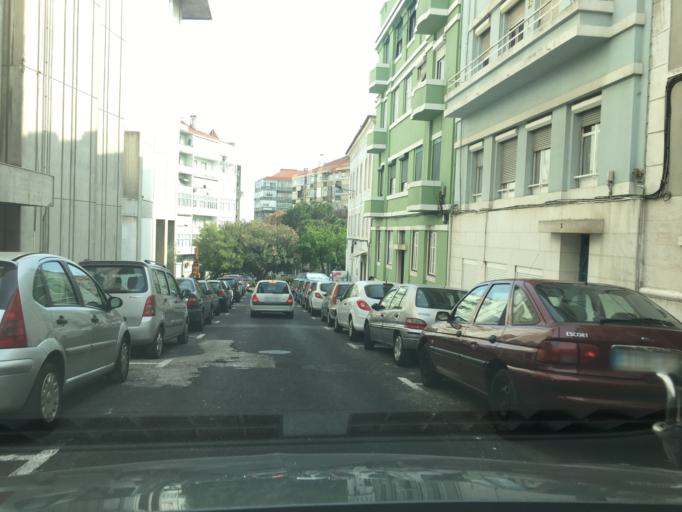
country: PT
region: Lisbon
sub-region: Lisbon
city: Lisbon
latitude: 38.7328
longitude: -9.1364
